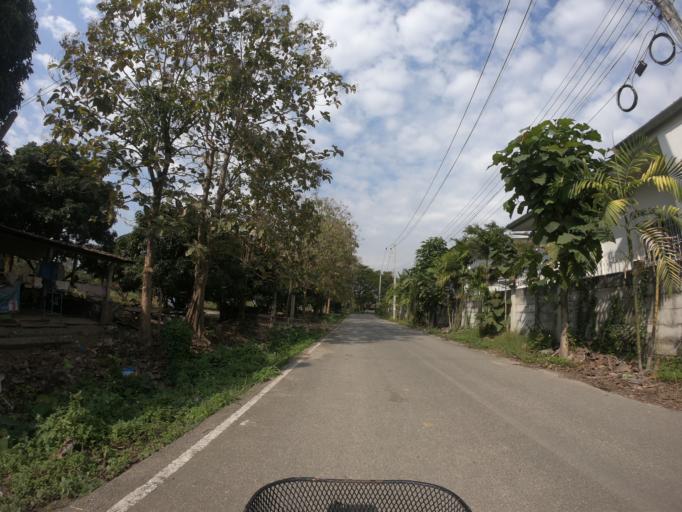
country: TH
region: Chiang Mai
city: Saraphi
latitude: 18.7416
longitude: 99.0611
